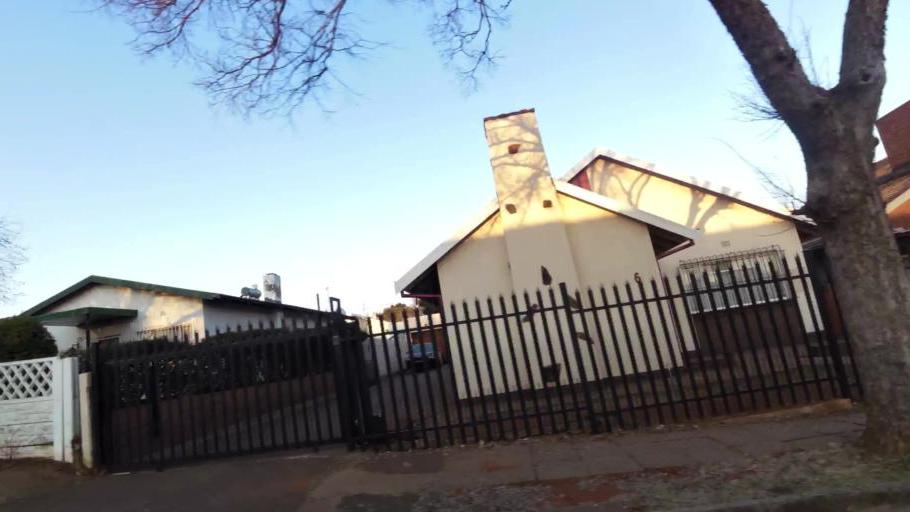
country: ZA
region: Gauteng
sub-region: City of Johannesburg Metropolitan Municipality
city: Roodepoort
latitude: -26.1863
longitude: 27.9514
